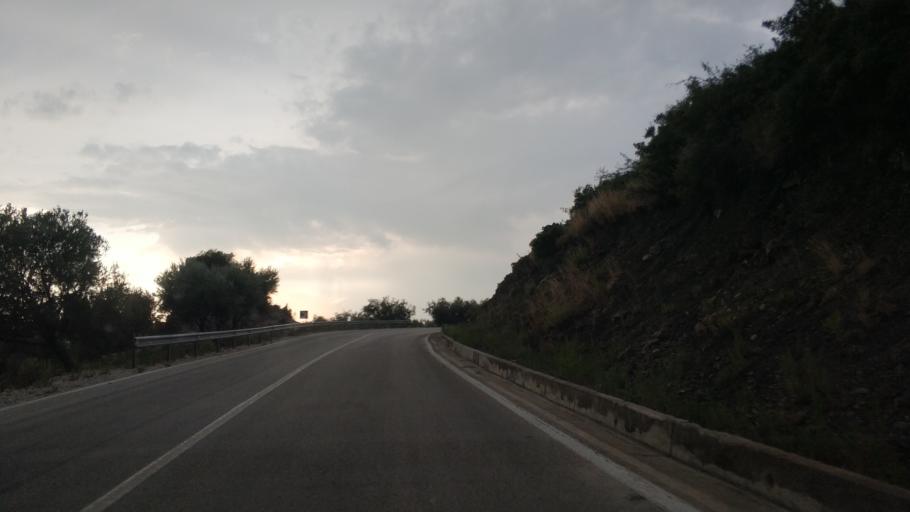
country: AL
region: Vlore
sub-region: Rrethi i Sarandes
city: Lukove
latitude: 40.0352
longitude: 19.8844
